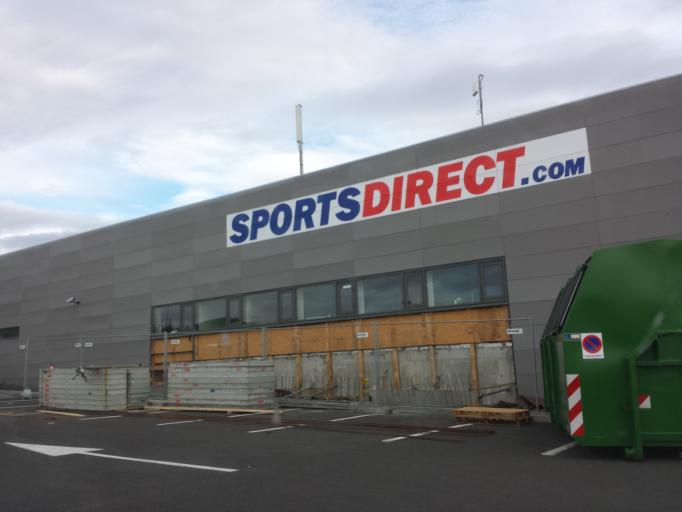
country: IS
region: Capital Region
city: Reykjavik
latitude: 64.1026
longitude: -21.8733
